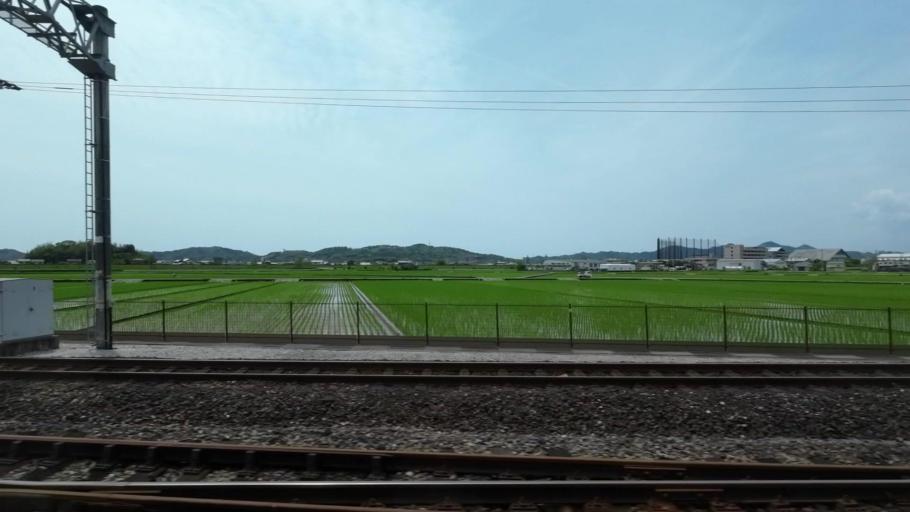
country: JP
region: Kochi
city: Kochi-shi
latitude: 33.5772
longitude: 133.5830
